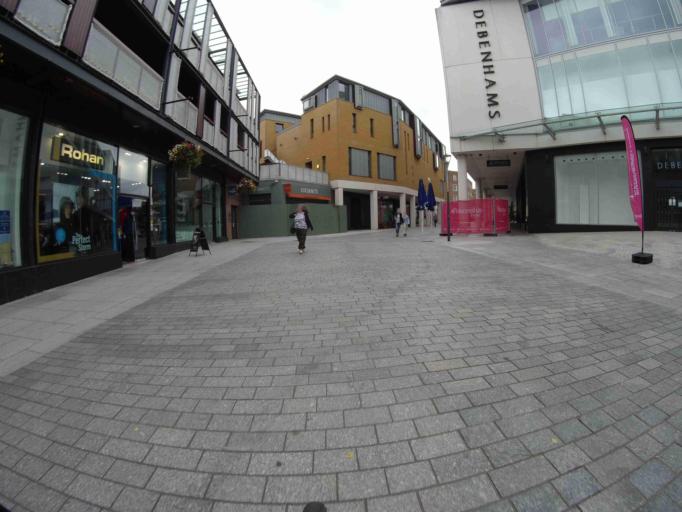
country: GB
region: England
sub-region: Devon
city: Exeter
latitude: 50.7233
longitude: -3.5275
